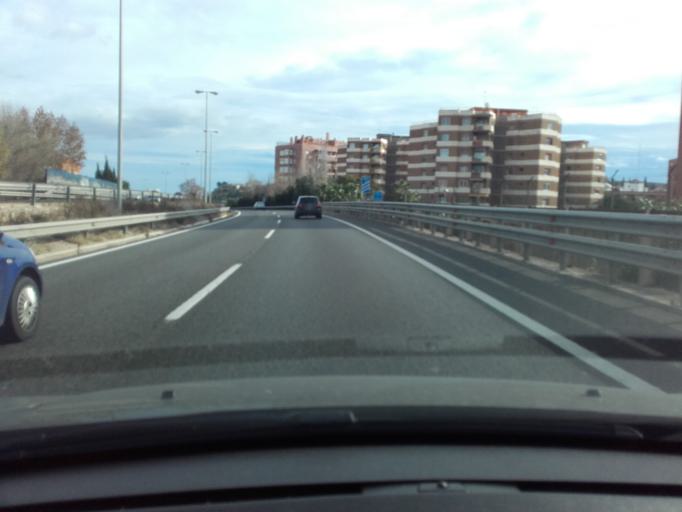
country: ES
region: Catalonia
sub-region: Provincia de Tarragona
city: Tarragona
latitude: 41.1237
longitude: 1.2515
